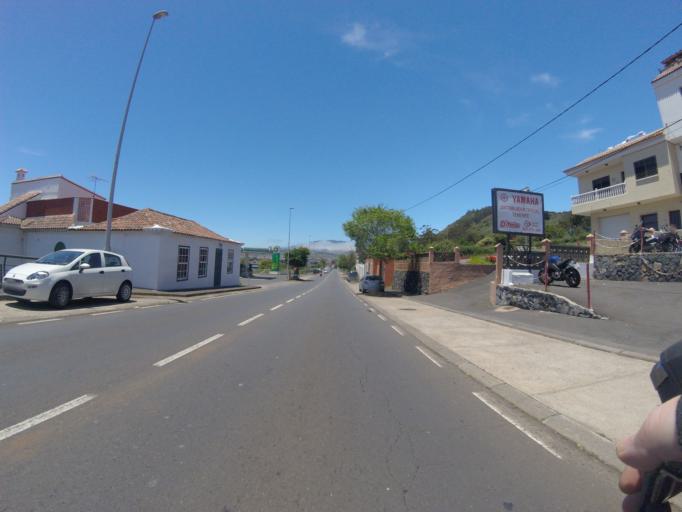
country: ES
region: Canary Islands
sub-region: Provincia de Santa Cruz de Tenerife
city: Tegueste
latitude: 28.5102
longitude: -16.3080
